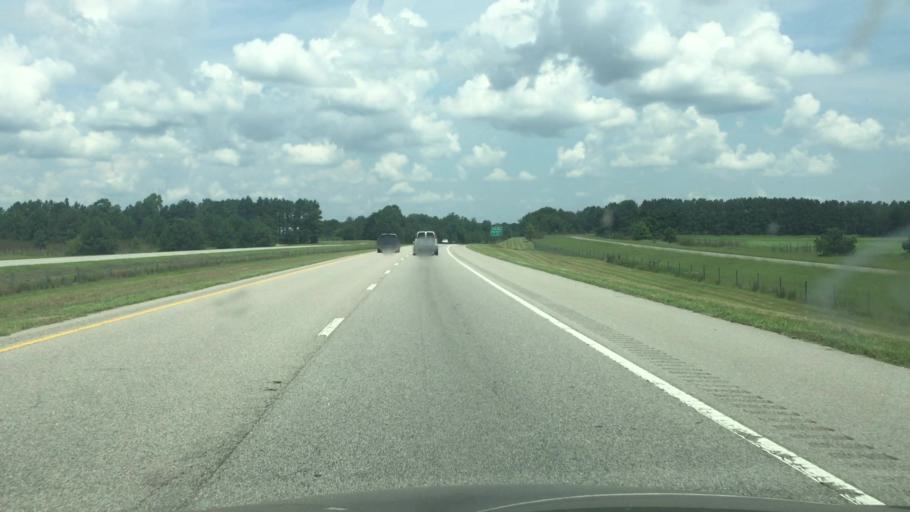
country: US
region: North Carolina
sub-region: Richmond County
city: Ellerbe
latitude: 35.1593
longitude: -79.7159
